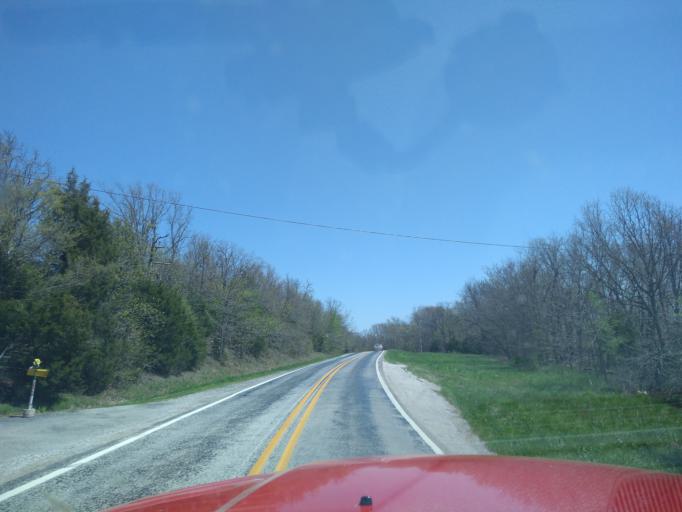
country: US
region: Arkansas
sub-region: Washington County
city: West Fork
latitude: 35.9046
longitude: -94.2033
